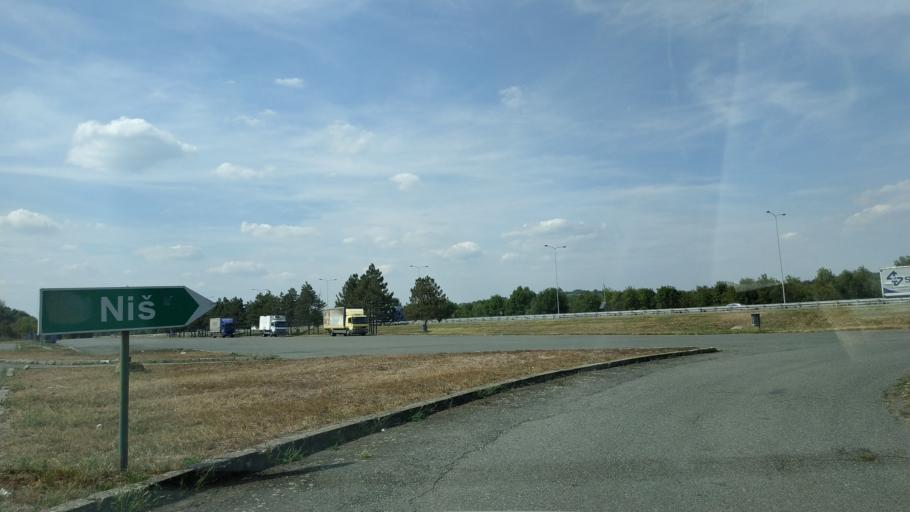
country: RS
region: Central Serbia
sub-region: Belgrade
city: Grocka
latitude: 44.5829
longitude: 20.8157
